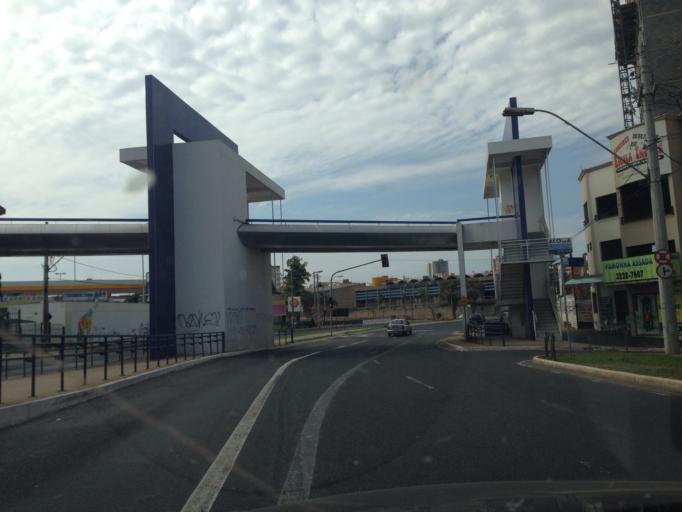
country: BR
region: Minas Gerais
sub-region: Uberlandia
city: Uberlandia
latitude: -18.9119
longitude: -48.2601
